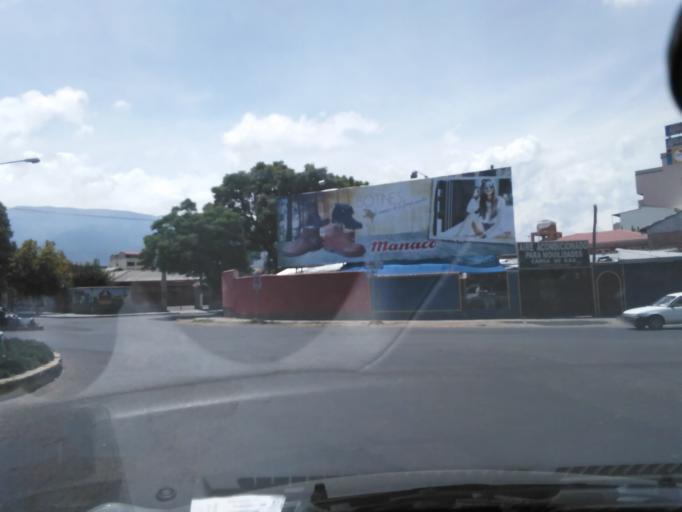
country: BO
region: Cochabamba
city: Cochabamba
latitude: -17.3972
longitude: -66.1673
